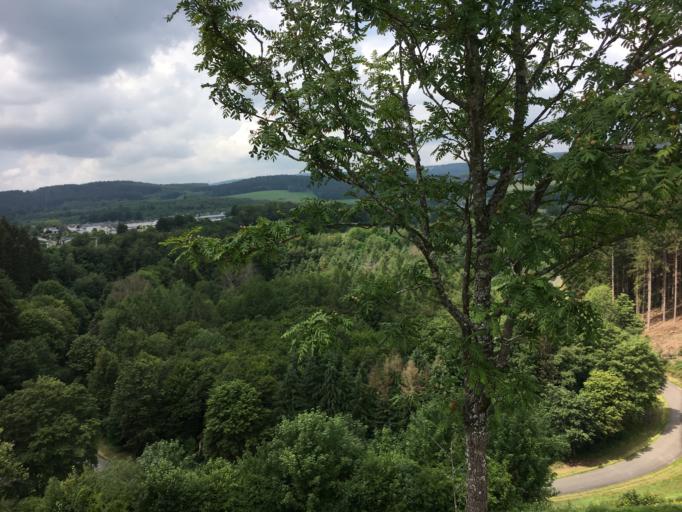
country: DE
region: North Rhine-Westphalia
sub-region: Regierungsbezirk Arnsberg
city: Attendorn
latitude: 51.1119
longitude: 7.8888
